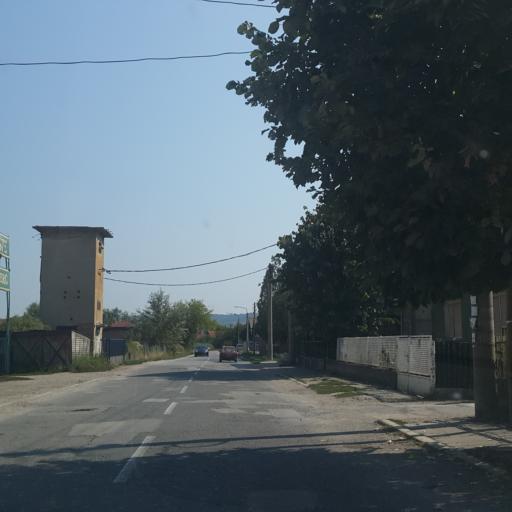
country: RS
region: Central Serbia
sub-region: Zajecarski Okrug
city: Zajecar
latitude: 43.9068
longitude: 22.2898
